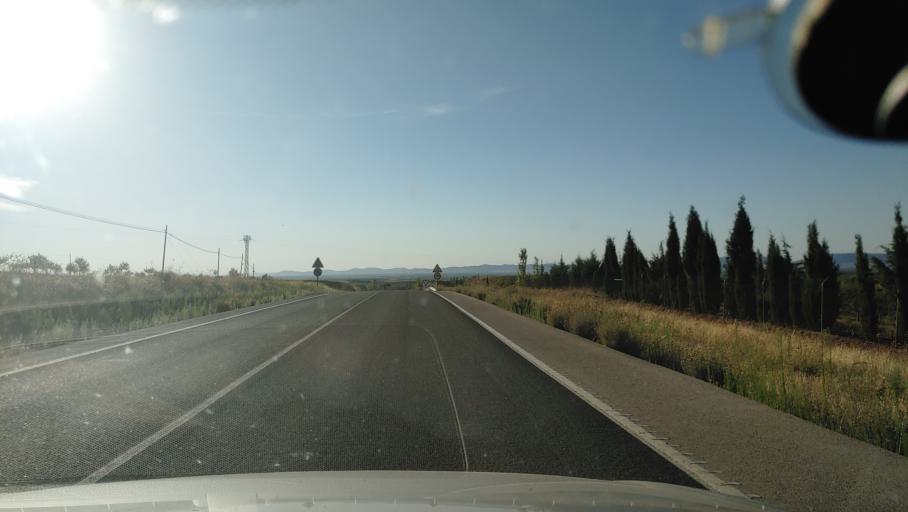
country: ES
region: Castille-La Mancha
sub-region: Provincia de Ciudad Real
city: Infantes
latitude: 38.7434
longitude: -2.9896
